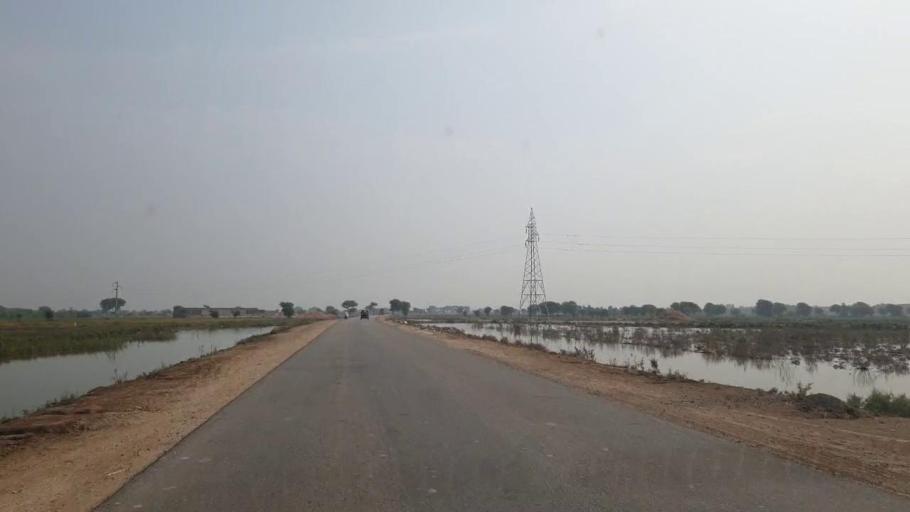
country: PK
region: Sindh
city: Matli
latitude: 25.0575
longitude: 68.6728
